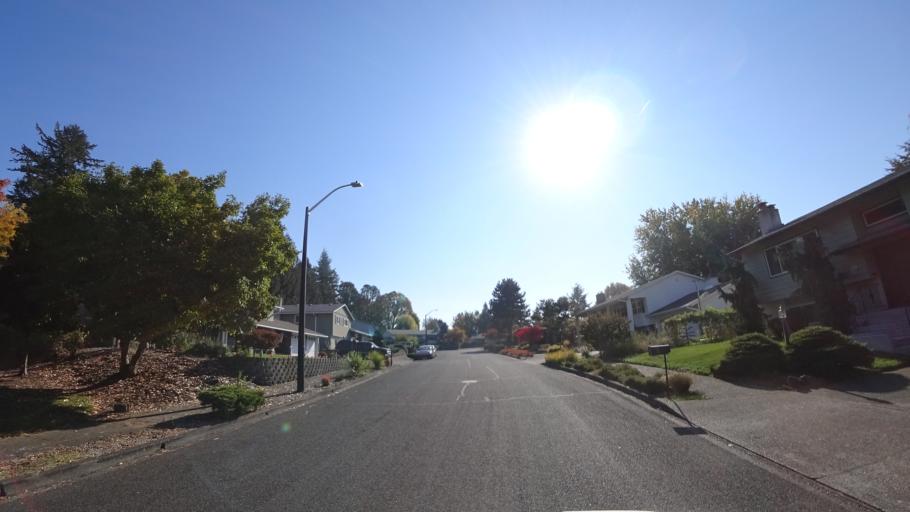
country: US
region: Oregon
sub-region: Multnomah County
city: Gresham
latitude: 45.5037
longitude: -122.4511
